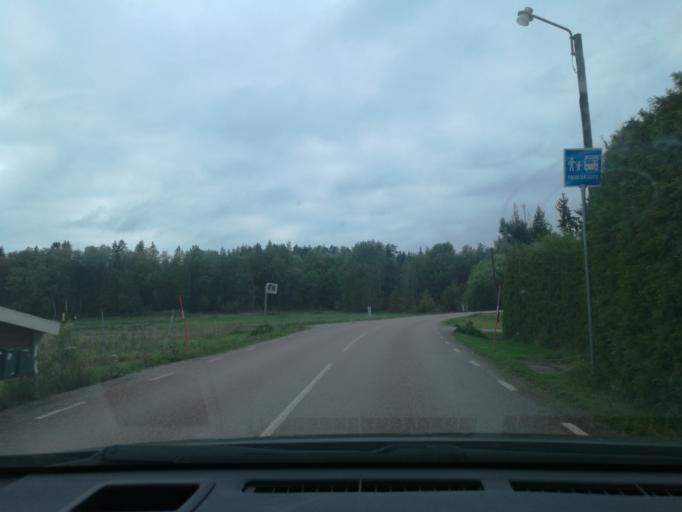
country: SE
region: Vaestmanland
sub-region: Vasteras
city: Tillberga
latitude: 59.6992
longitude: 16.6469
